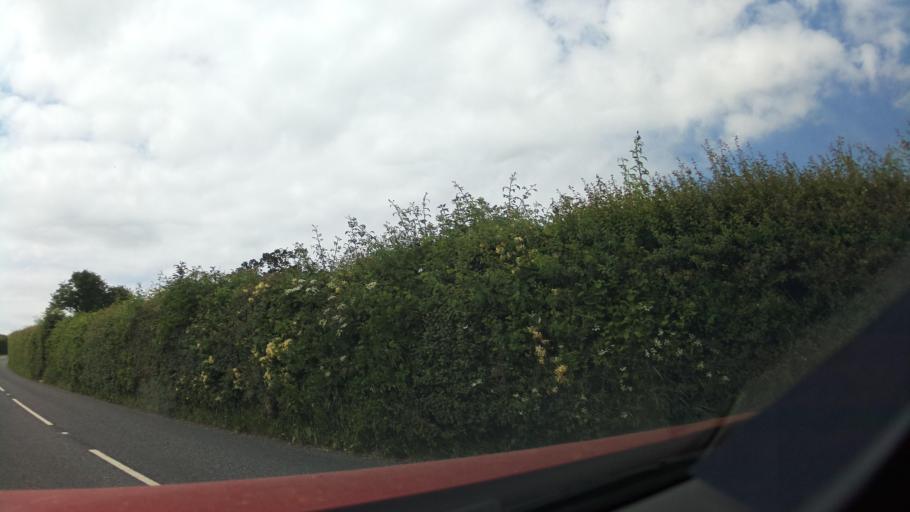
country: GB
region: England
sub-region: Somerset
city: Milborne Port
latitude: 51.0264
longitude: -2.4619
